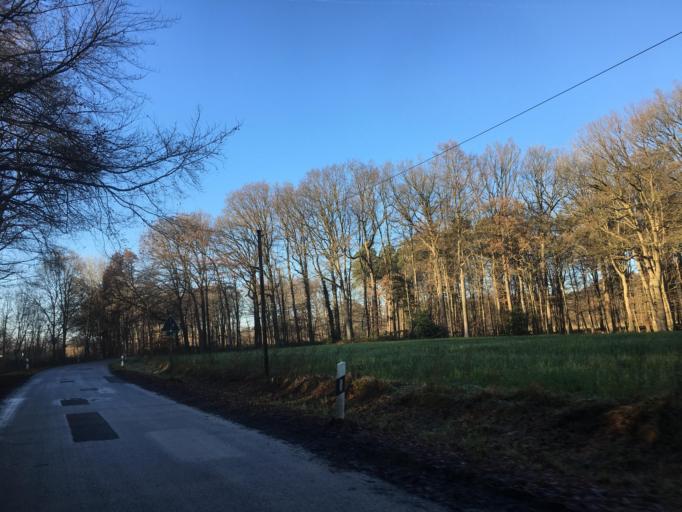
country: DE
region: North Rhine-Westphalia
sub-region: Regierungsbezirk Munster
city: Dulmen
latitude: 51.8055
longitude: 7.3484
